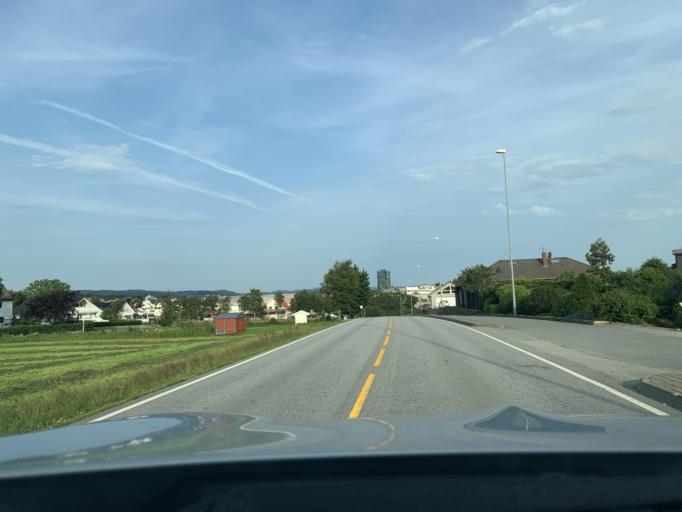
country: NO
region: Rogaland
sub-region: Time
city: Bryne
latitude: 58.7380
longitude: 5.6316
